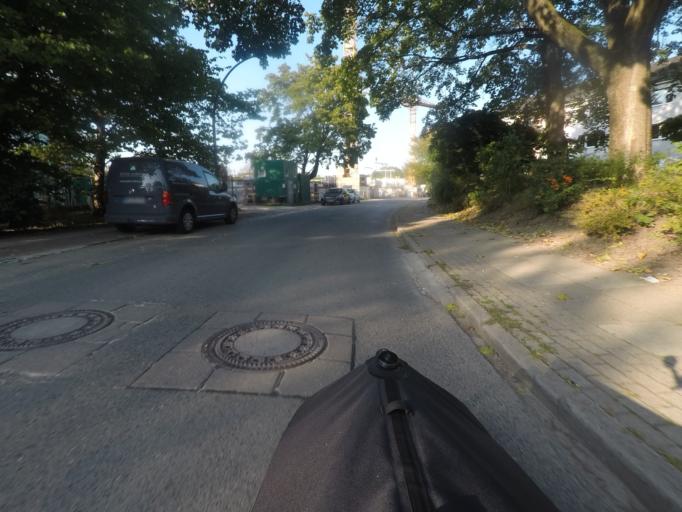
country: DE
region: Hamburg
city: Farmsen-Berne
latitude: 53.6115
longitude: 10.1639
